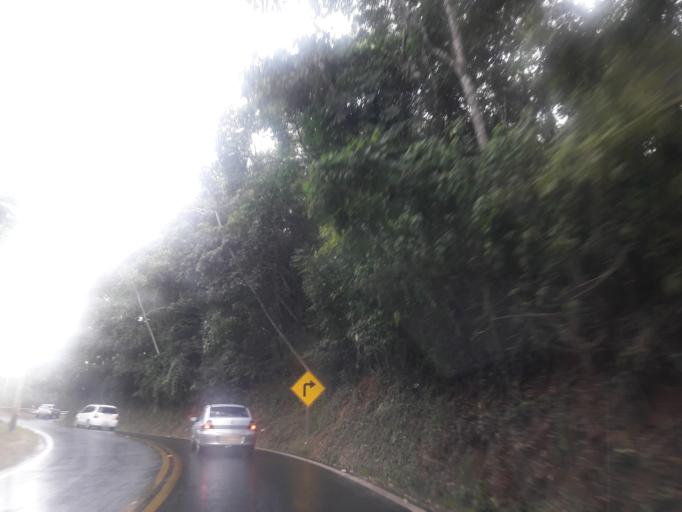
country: BR
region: Sao Paulo
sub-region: Aruja
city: Aruja
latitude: -23.3243
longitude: -46.4329
